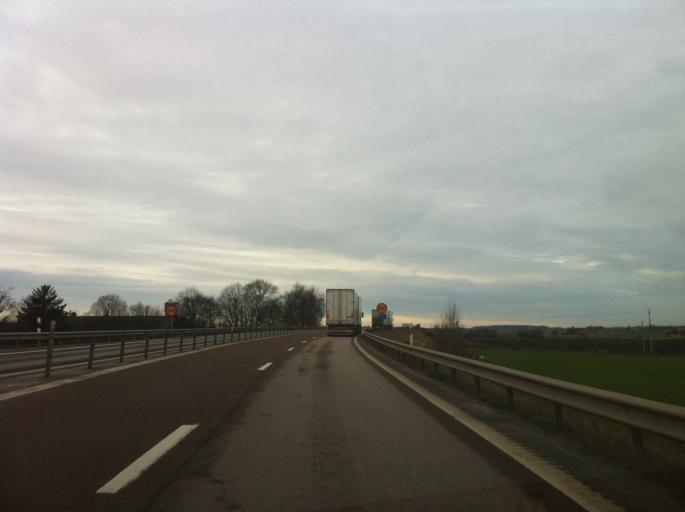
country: SE
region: Skane
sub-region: Astorps Kommun
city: Astorp
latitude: 56.1359
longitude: 12.9968
